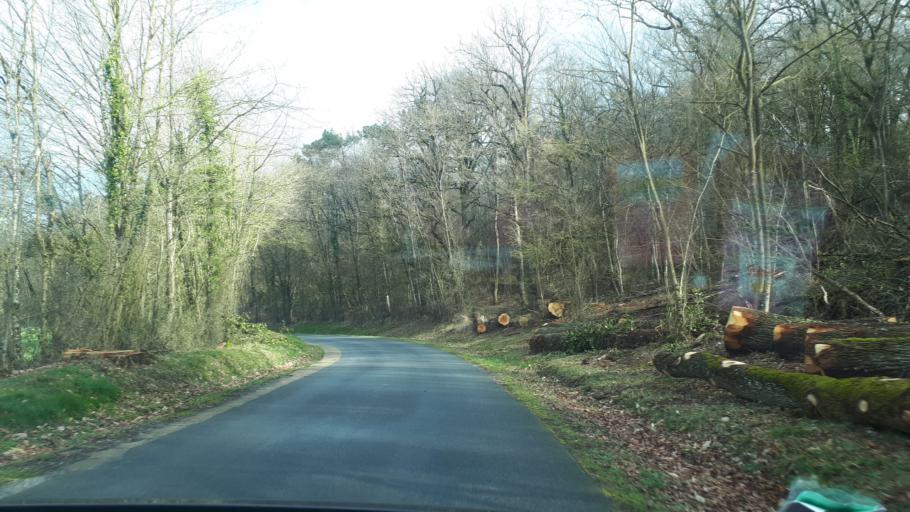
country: FR
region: Centre
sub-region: Departement du Loir-et-Cher
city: Sarge-sur-Braye
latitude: 47.9100
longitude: 0.8708
